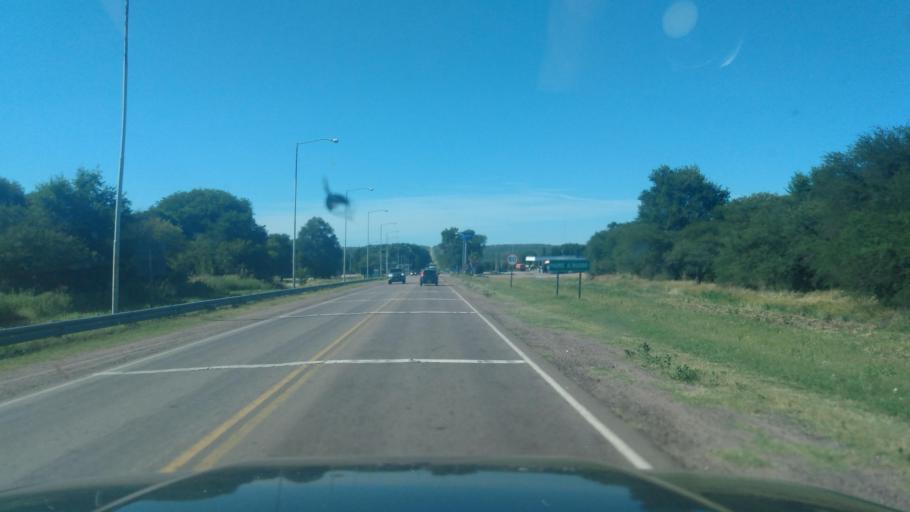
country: AR
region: La Pampa
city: Doblas
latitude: -37.3044
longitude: -64.2879
